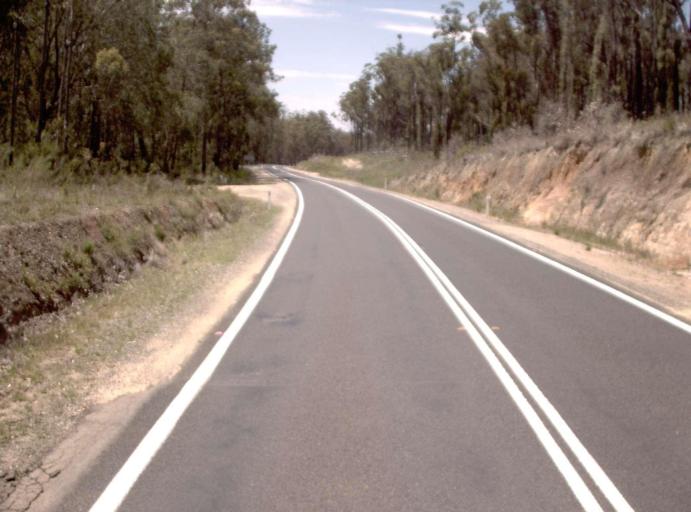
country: AU
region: New South Wales
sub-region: Bombala
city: Bombala
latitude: -37.6388
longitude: 148.8509
